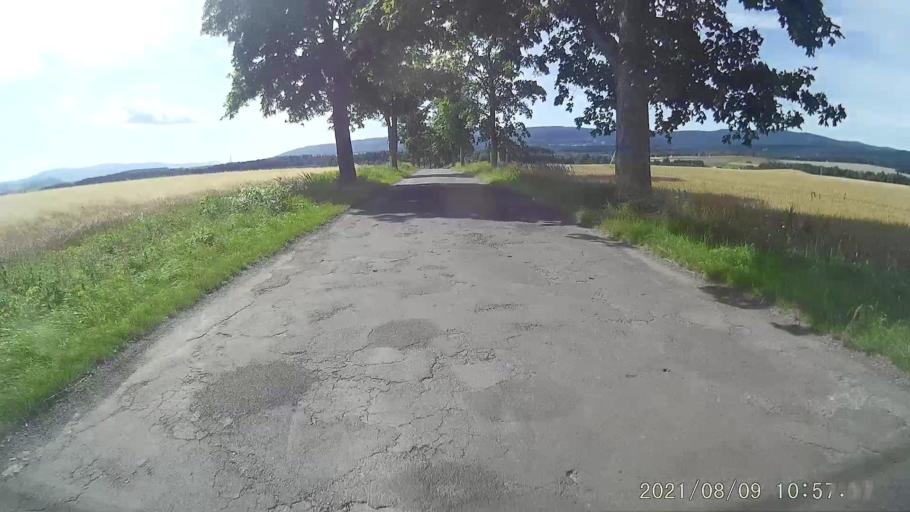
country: PL
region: Lower Silesian Voivodeship
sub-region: Powiat klodzki
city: Polanica-Zdroj
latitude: 50.4392
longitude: 16.5485
